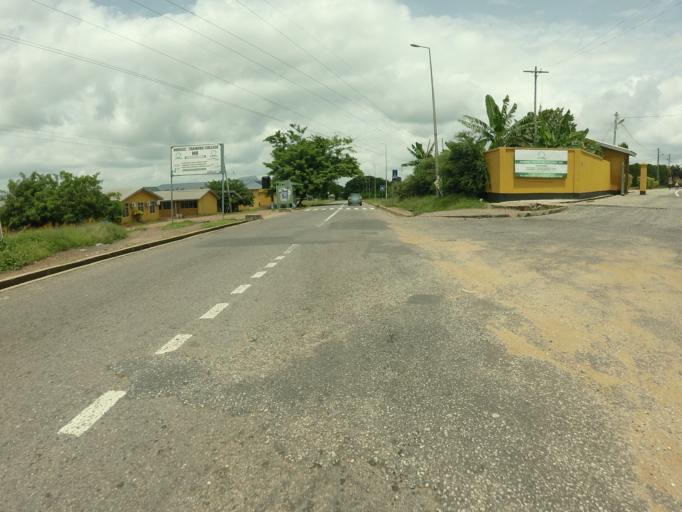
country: GH
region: Volta
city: Ho
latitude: 6.6004
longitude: 0.4798
